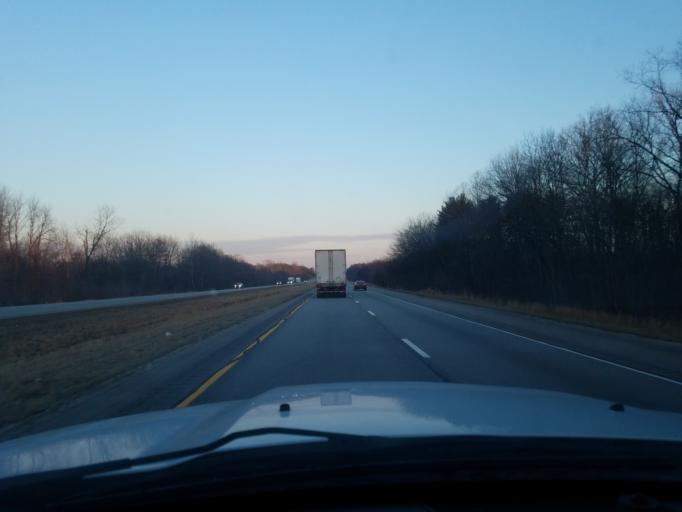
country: US
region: Indiana
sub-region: Gibson County
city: Oakland City
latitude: 38.1924
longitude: -87.3360
